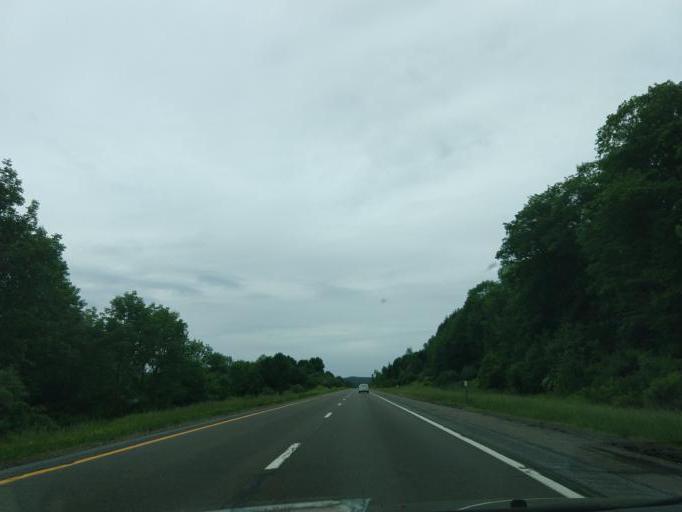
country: US
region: New York
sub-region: Broome County
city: Chenango Bridge
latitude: 42.2707
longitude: -75.9241
